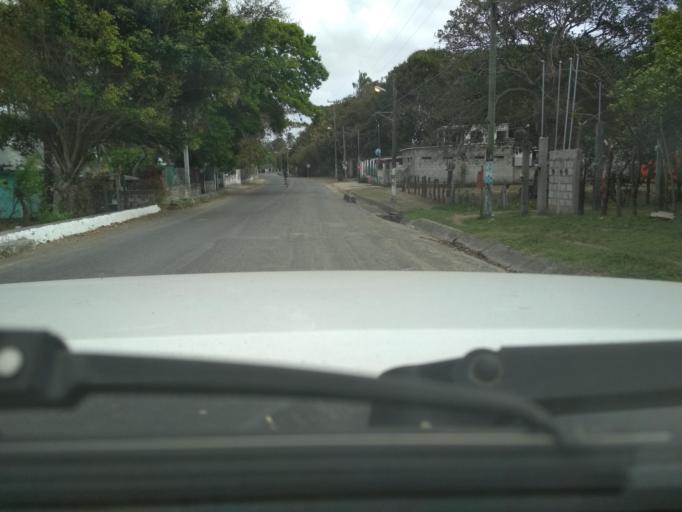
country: MX
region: Veracruz
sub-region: Veracruz
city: Delfino Victoria (Santa Fe)
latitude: 19.2503
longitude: -96.2607
